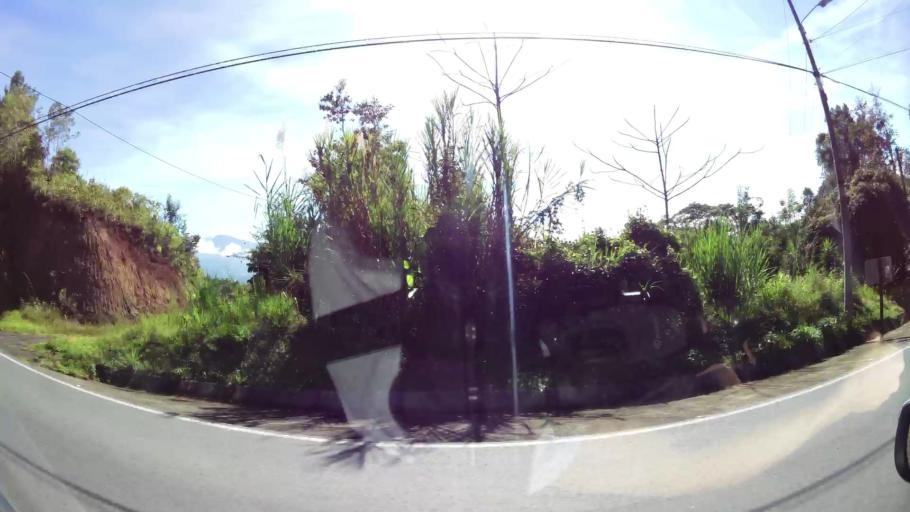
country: CR
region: San Jose
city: San Isidro
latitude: 9.4143
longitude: -83.7138
